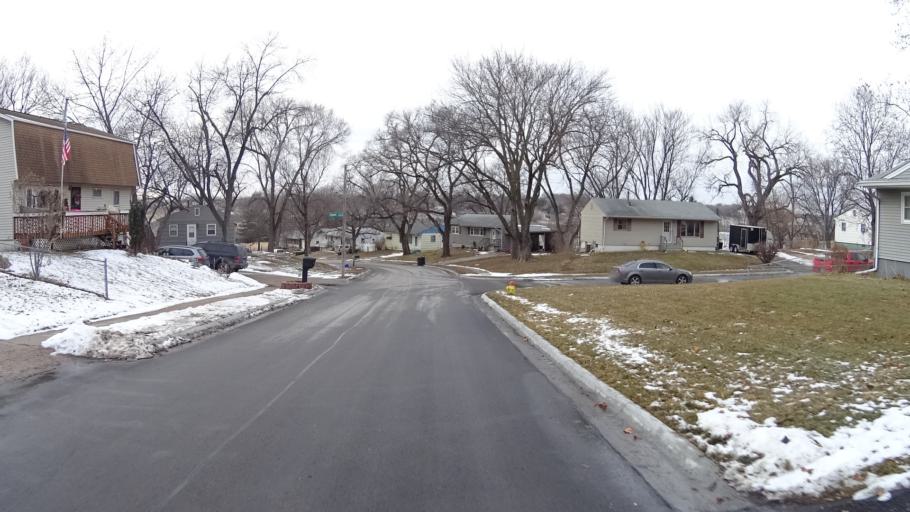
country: US
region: Nebraska
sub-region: Sarpy County
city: Offutt Air Force Base
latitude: 41.1587
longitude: -95.9233
